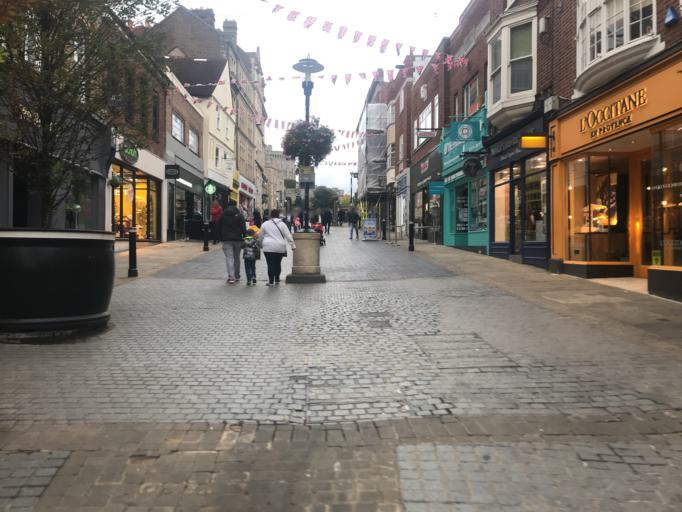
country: GB
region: England
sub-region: West Berkshire
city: Eton
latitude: 51.4820
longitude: -0.6085
